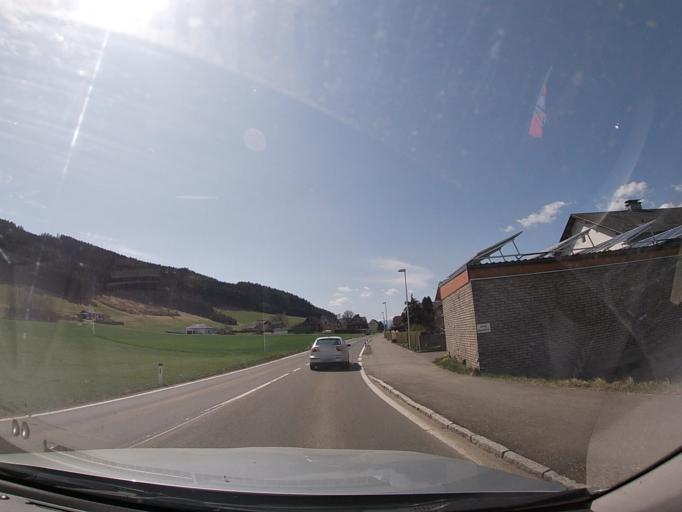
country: AT
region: Styria
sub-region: Politischer Bezirk Murtal
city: Sankt Margarethen bei Knittelfeld
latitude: 47.2344
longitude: 14.8691
